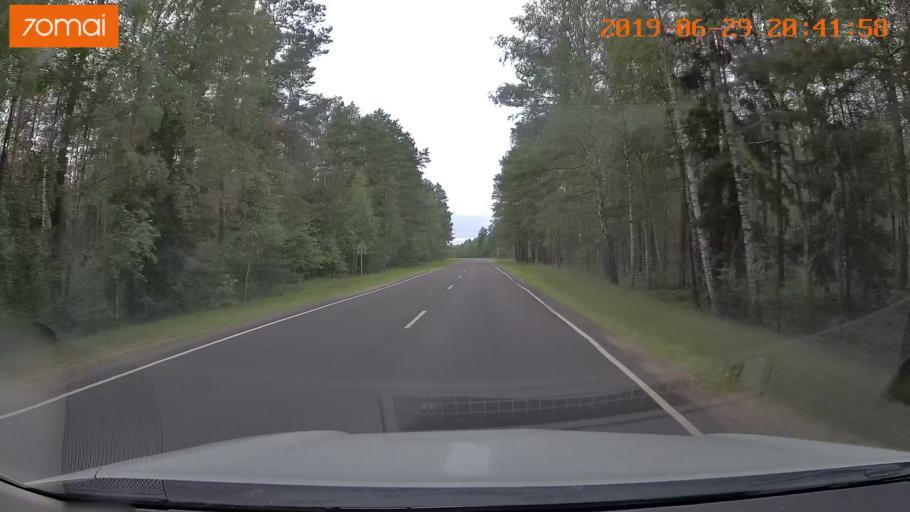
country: BY
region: Brest
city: Hantsavichy
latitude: 52.5920
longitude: 26.3327
